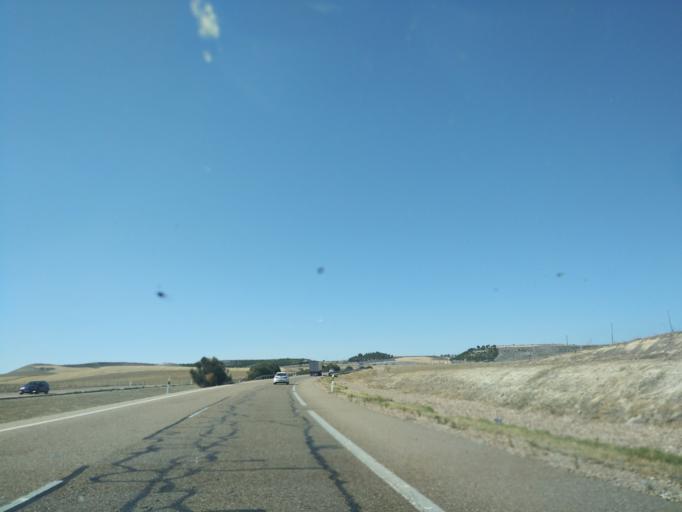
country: ES
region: Castille and Leon
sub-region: Provincia de Valladolid
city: Mota del Marques
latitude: 41.6504
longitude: -5.1909
